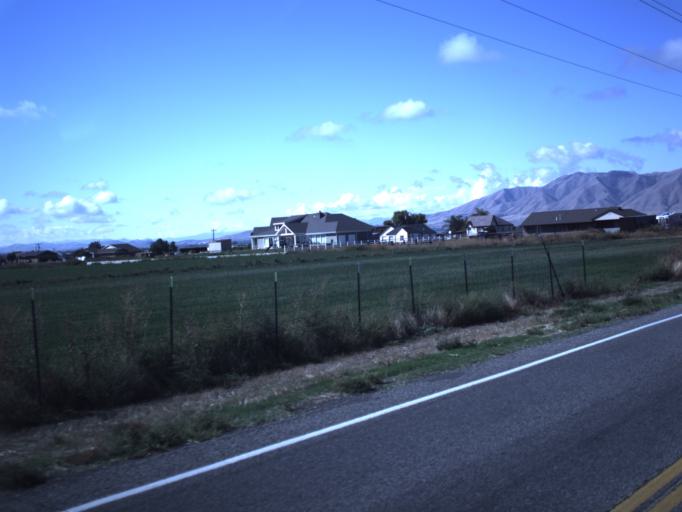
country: US
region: Utah
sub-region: Utah County
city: Benjamin
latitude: 40.0983
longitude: -111.6959
